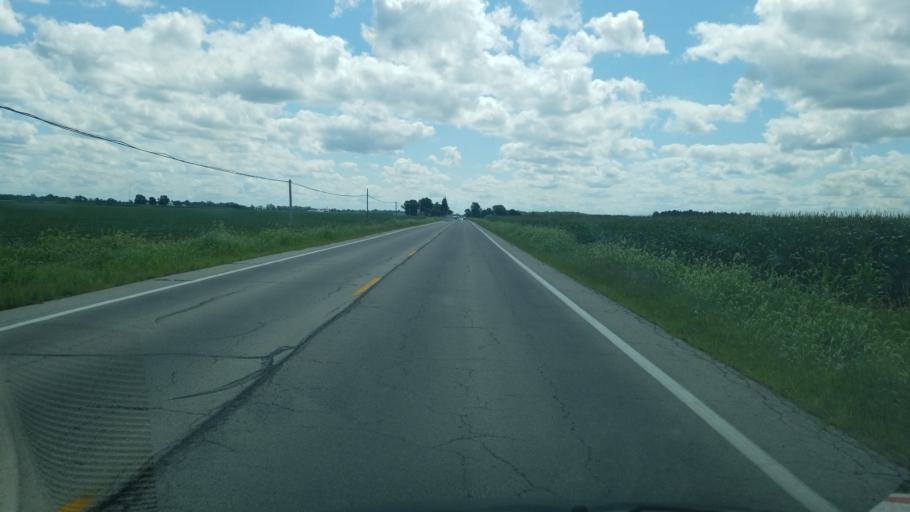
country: US
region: Ohio
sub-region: Henry County
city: Napoleon
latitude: 41.3522
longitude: -84.1198
